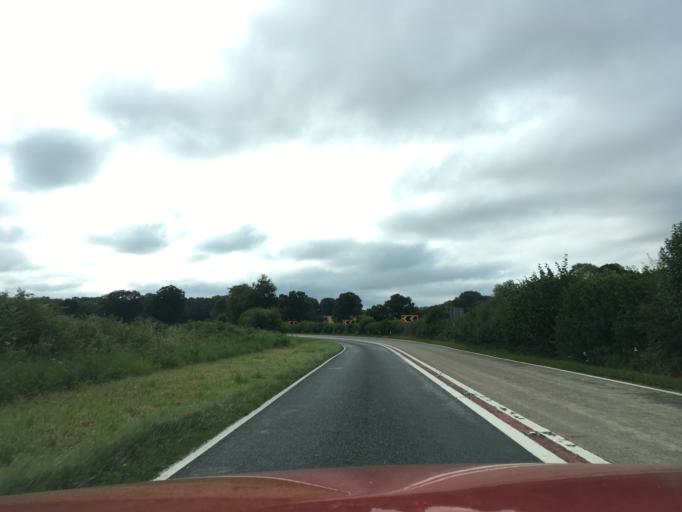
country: GB
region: England
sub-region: Hampshire
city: Four Marks
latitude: 51.0316
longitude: -1.0429
